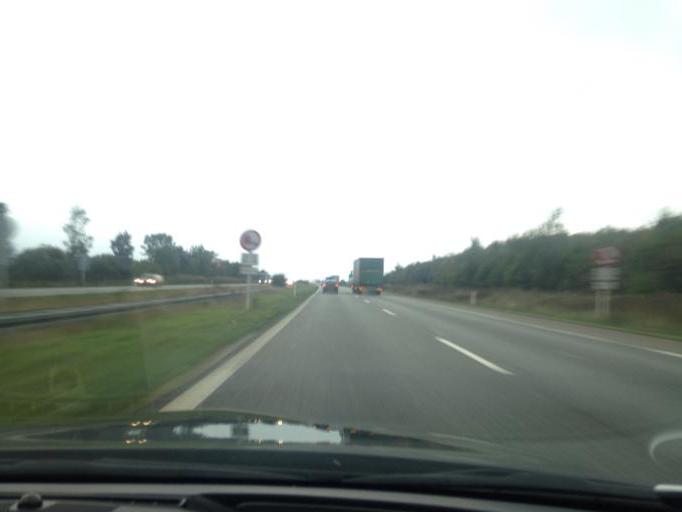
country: DK
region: South Denmark
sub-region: Kolding Kommune
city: Christiansfeld
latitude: 55.3663
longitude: 9.4507
